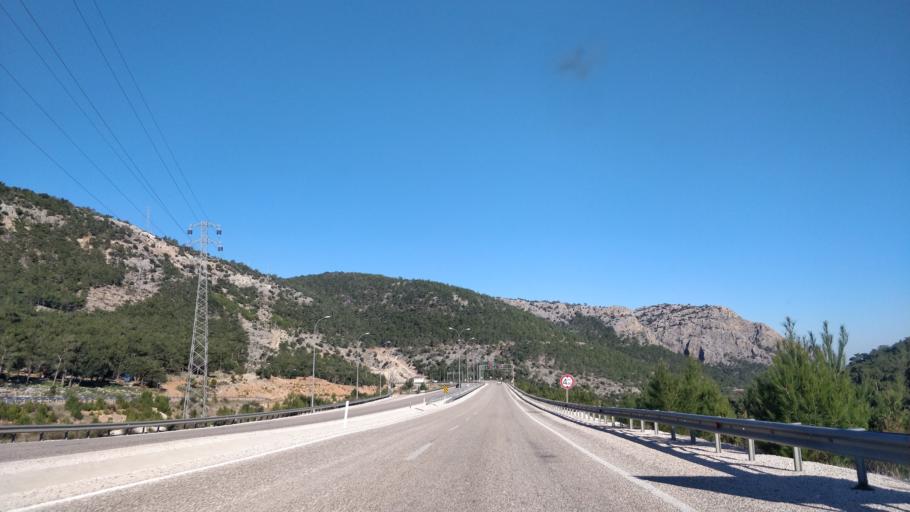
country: TR
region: Mersin
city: Akdere
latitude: 36.2547
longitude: 33.7840
